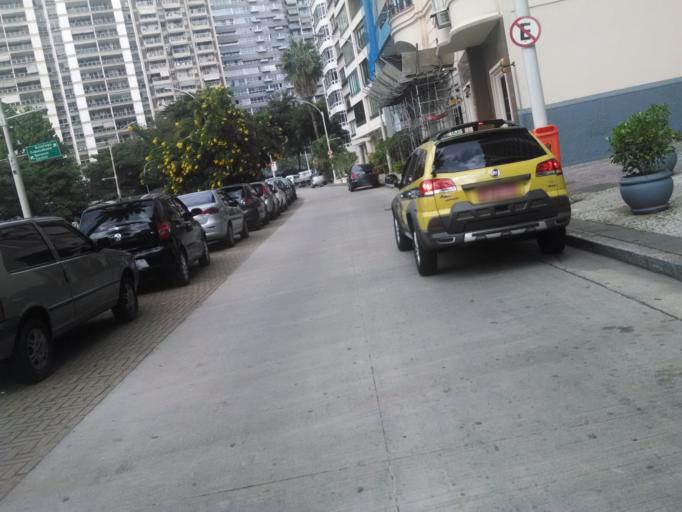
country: BR
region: Rio de Janeiro
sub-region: Rio De Janeiro
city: Rio de Janeiro
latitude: -22.9374
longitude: -43.1740
